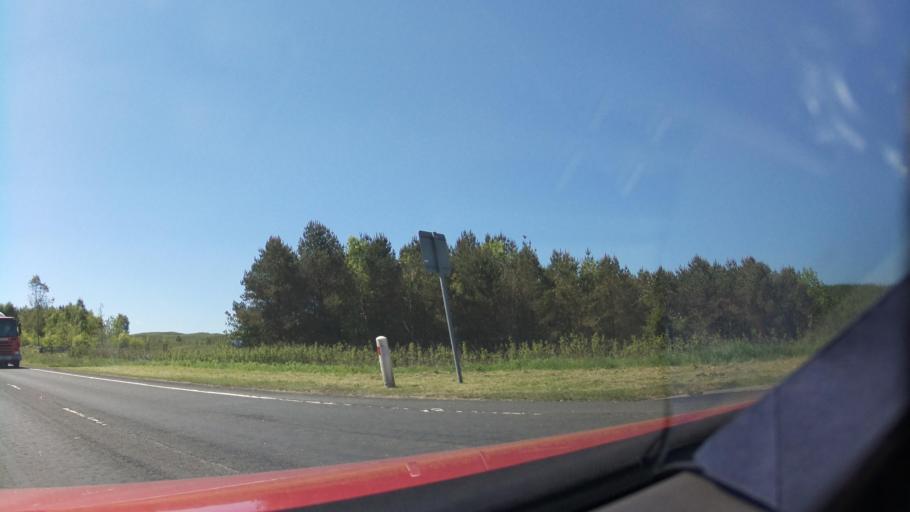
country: GB
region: Scotland
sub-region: The Scottish Borders
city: Selkirk
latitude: 55.5155
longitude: -2.8453
